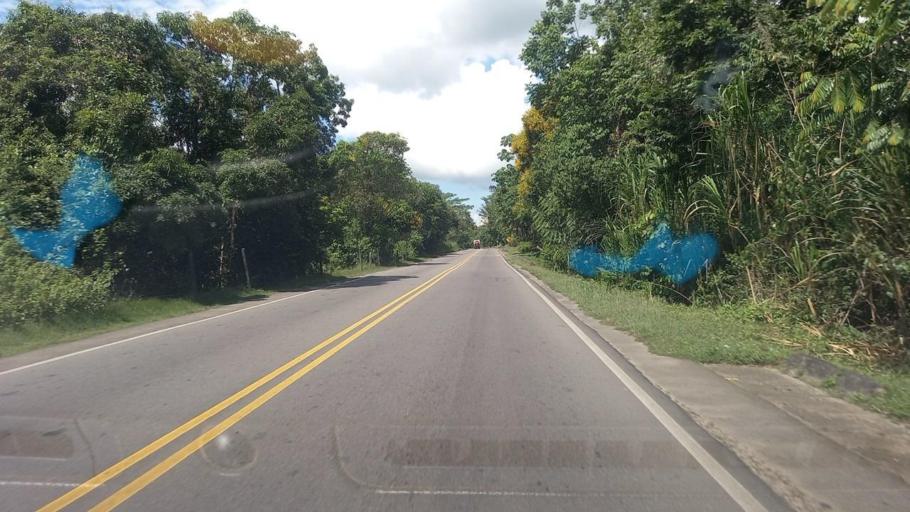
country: CO
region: Santander
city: Barrancabermeja
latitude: 7.1202
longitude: -73.6048
